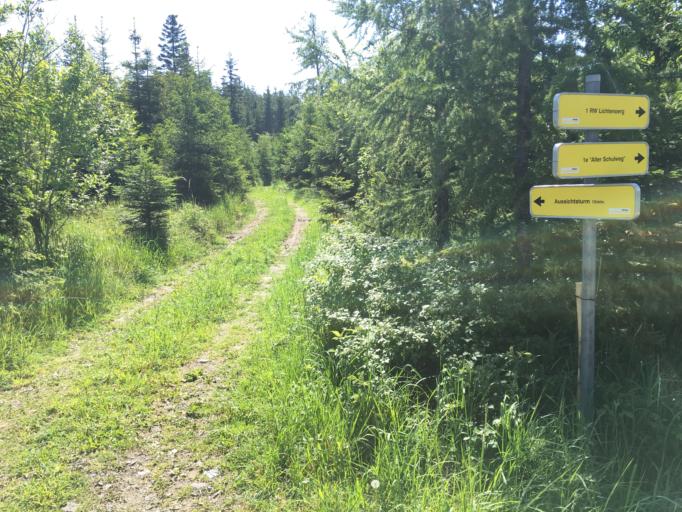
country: AT
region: Upper Austria
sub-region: Politischer Bezirk Vocklabruck
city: Frankenmarkt
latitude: 47.9347
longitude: 13.4194
